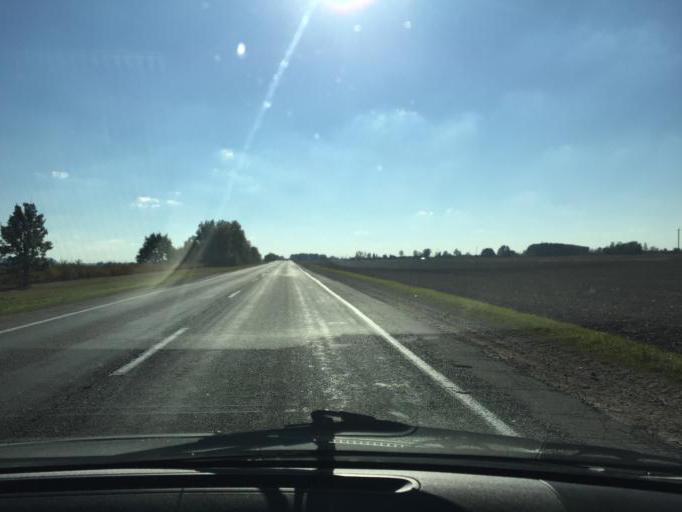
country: BY
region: Minsk
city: Slutsk
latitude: 52.9232
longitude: 27.4842
